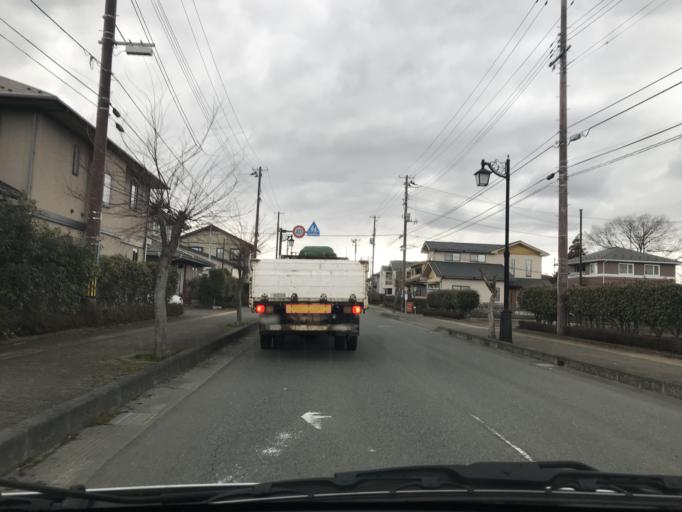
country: JP
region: Iwate
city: Mizusawa
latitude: 39.1146
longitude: 141.1655
